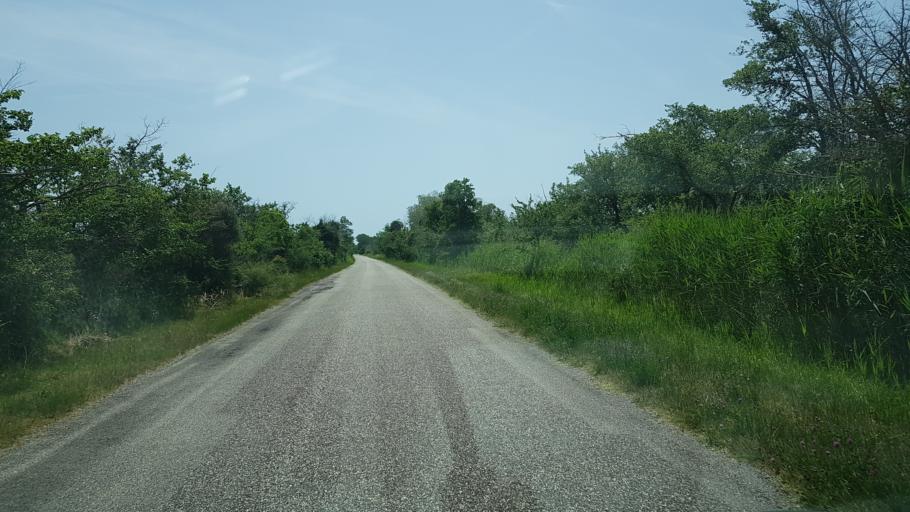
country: FR
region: Provence-Alpes-Cote d'Azur
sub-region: Departement des Bouches-du-Rhone
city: Port-Saint-Louis-du-Rhone
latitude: 43.4636
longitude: 4.6537
